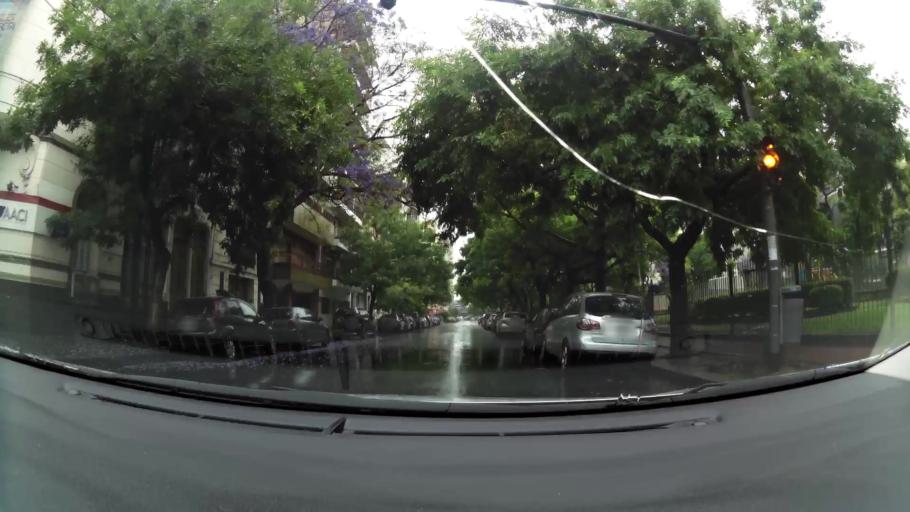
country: AR
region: Buenos Aires
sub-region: Partido de Avellaneda
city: Avellaneda
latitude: -34.6377
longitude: -58.3737
